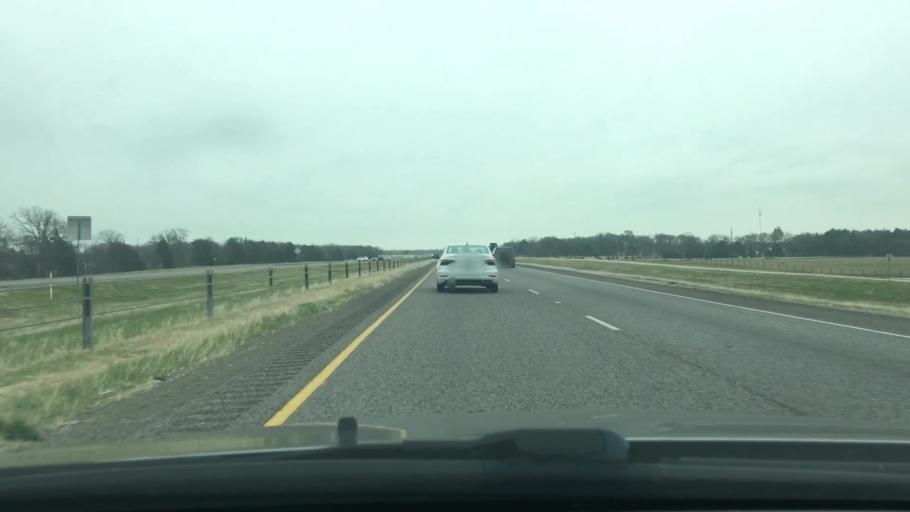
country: US
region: Texas
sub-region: Freestone County
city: Fairfield
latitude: 31.7710
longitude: -96.2214
